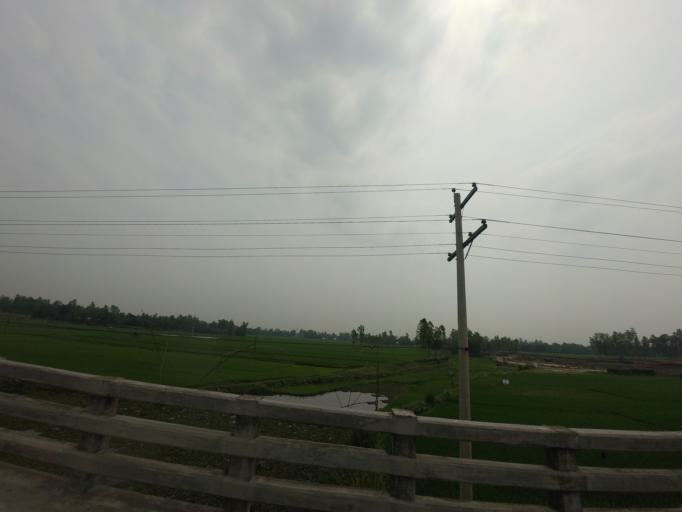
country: BD
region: Rajshahi
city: Sirajganj
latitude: 24.3650
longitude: 89.6709
